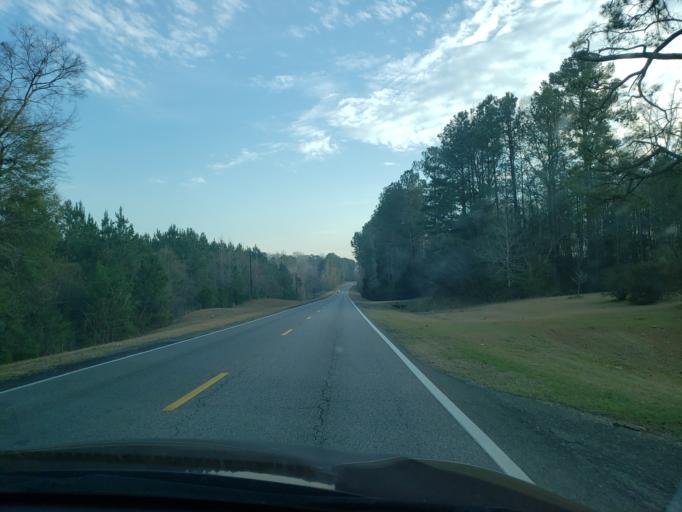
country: US
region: Alabama
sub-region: Hale County
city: Greensboro
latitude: 32.7397
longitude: -87.5856
